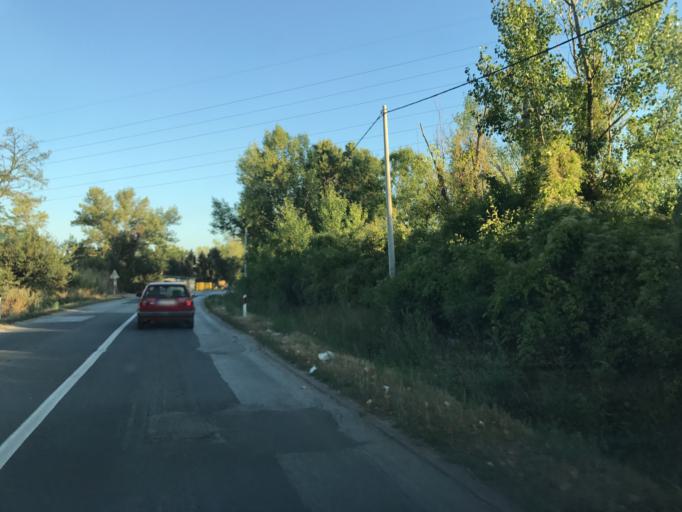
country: RS
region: Central Serbia
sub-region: Podunavski Okrug
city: Smederevo
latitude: 44.5861
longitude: 20.9751
